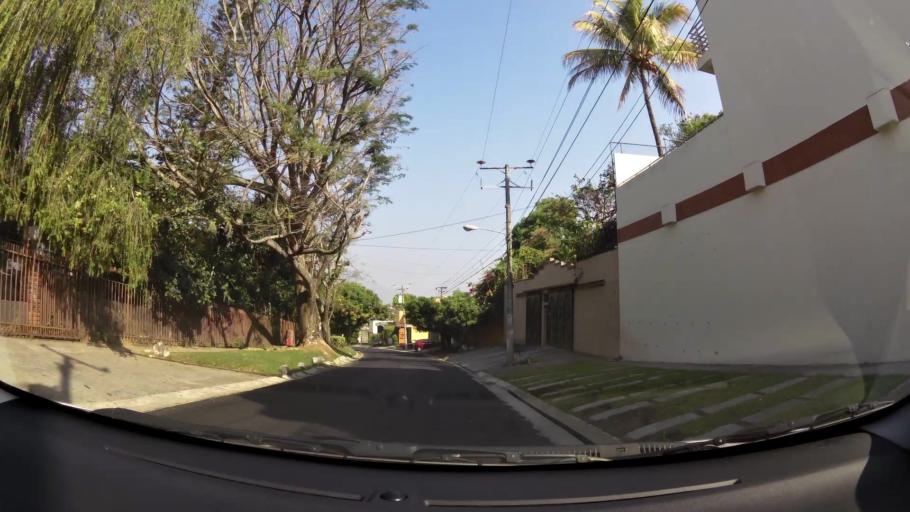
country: SV
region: La Libertad
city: Antiguo Cuscatlan
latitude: 13.6710
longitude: -89.2311
